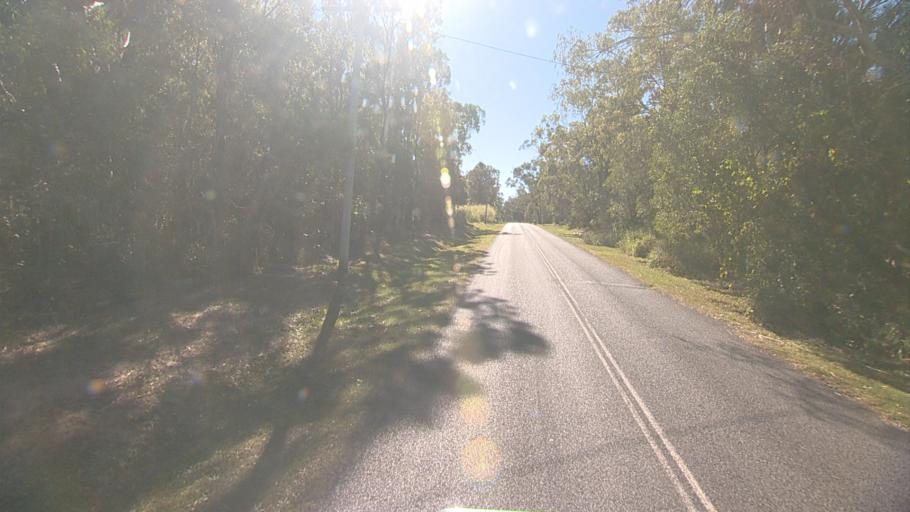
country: AU
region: Queensland
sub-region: Logan
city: Park Ridge South
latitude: -27.7137
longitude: 153.0582
